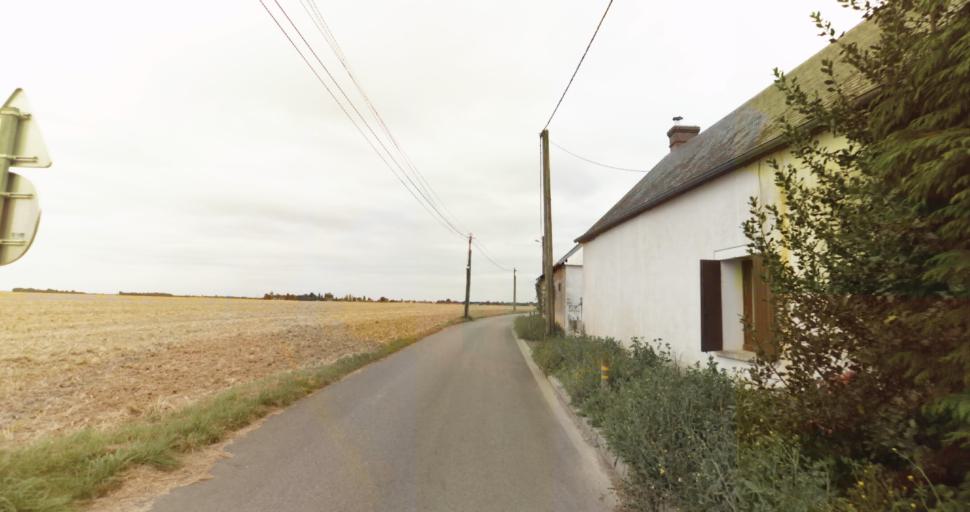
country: FR
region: Haute-Normandie
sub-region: Departement de l'Eure
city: Marcilly-sur-Eure
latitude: 48.9133
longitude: 1.3010
